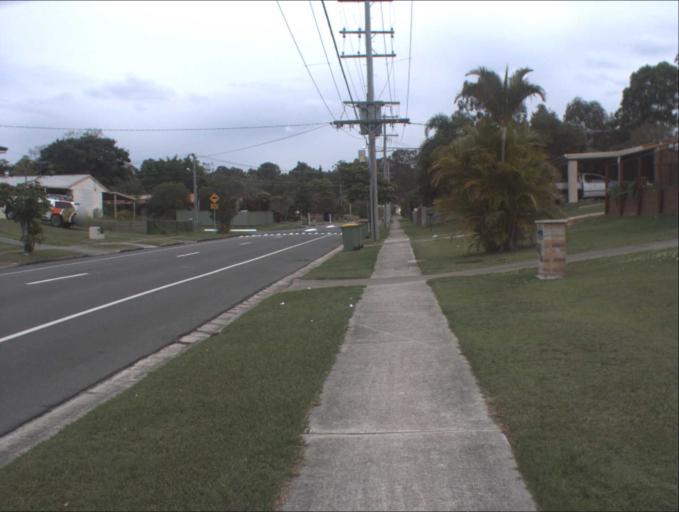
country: AU
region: Queensland
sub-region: Logan
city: Park Ridge South
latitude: -27.6833
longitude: 153.0289
